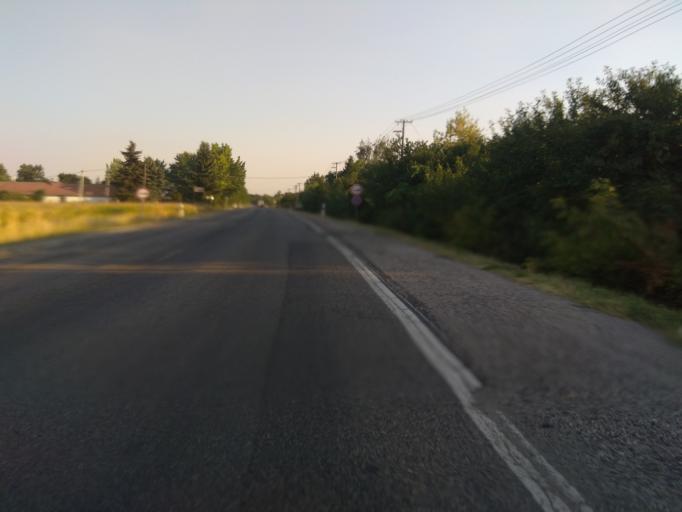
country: HU
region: Borsod-Abauj-Zemplen
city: Nyekladhaza
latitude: 47.9745
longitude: 20.8301
